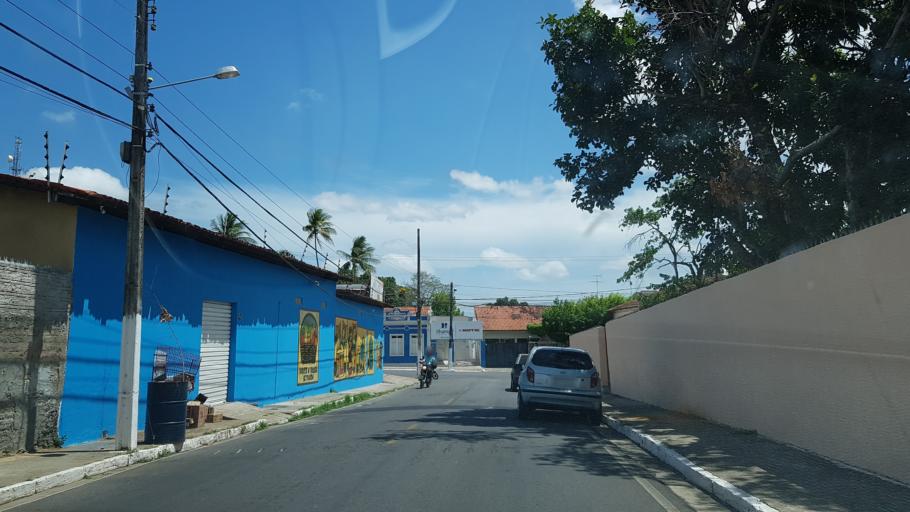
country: BR
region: Alagoas
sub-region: Penedo
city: Penedo
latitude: -10.2835
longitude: -36.5727
